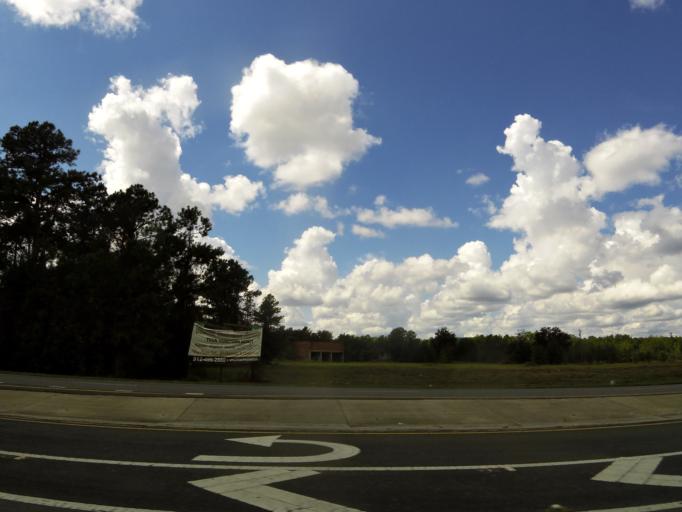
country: US
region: Georgia
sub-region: Charlton County
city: Folkston
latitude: 30.8423
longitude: -82.0066
